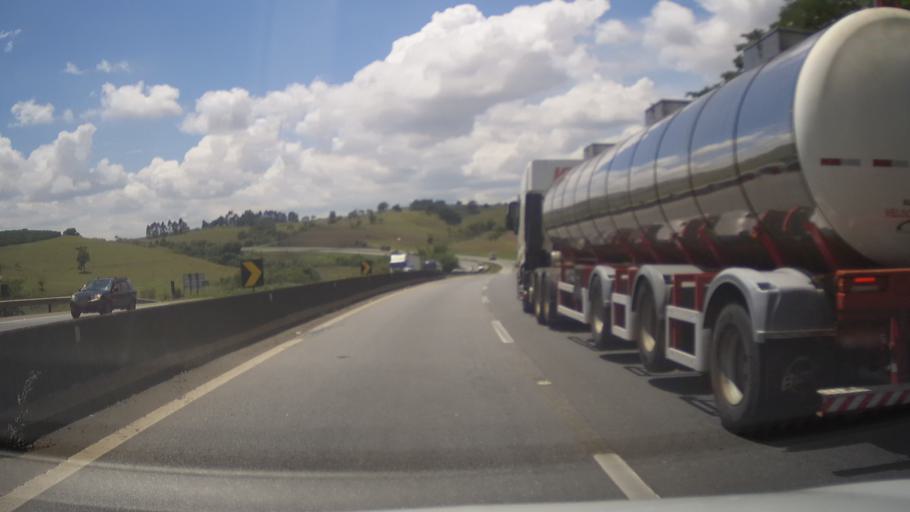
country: BR
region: Minas Gerais
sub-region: Sao Goncalo Do Sapucai
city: Sao Goncalo do Sapucai
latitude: -21.9089
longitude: -45.5695
